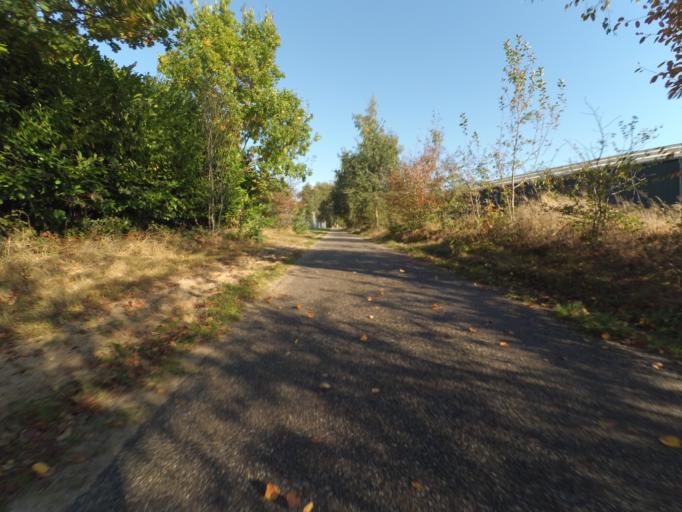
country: NL
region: Gelderland
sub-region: Gemeente Epe
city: Vaassen
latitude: 52.2804
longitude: 5.9713
